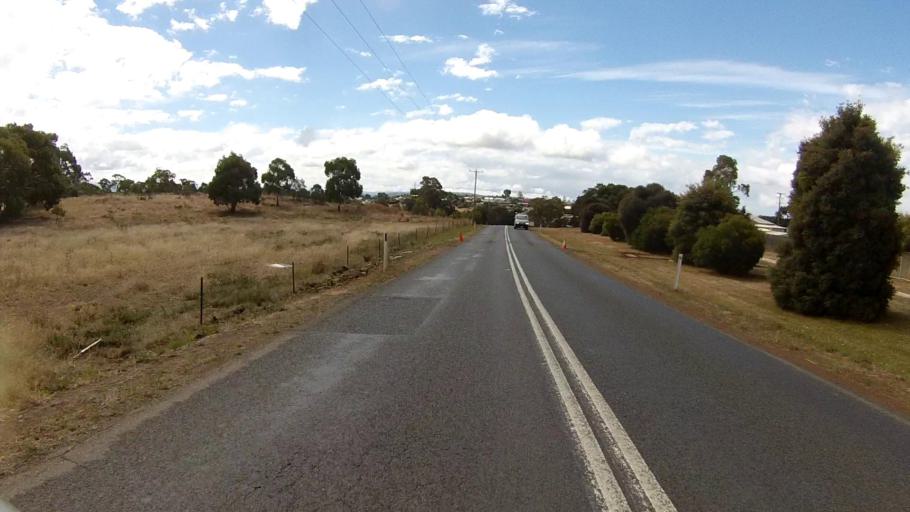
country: AU
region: Tasmania
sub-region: Sorell
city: Sorell
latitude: -42.1333
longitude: 148.0714
